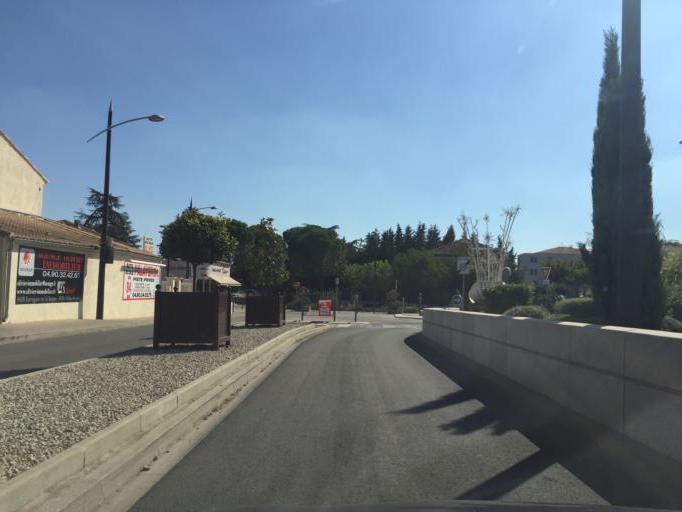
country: FR
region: Provence-Alpes-Cote d'Azur
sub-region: Departement du Vaucluse
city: Monteux
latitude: 44.0336
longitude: 4.9914
